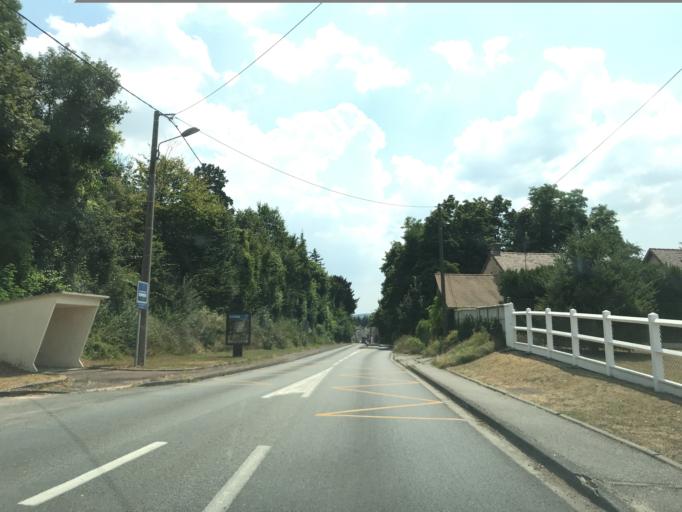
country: FR
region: Haute-Normandie
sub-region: Departement de l'Eure
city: Breuilpont
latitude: 48.9660
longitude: 1.4261
